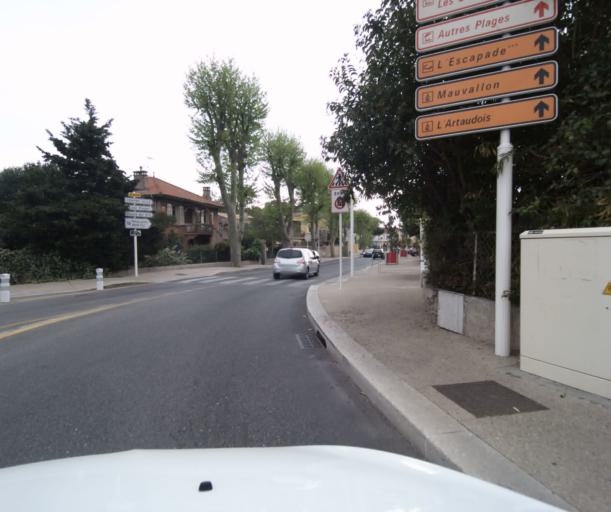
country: FR
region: Provence-Alpes-Cote d'Azur
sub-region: Departement du Var
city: Le Pradet
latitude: 43.1068
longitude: 6.0251
